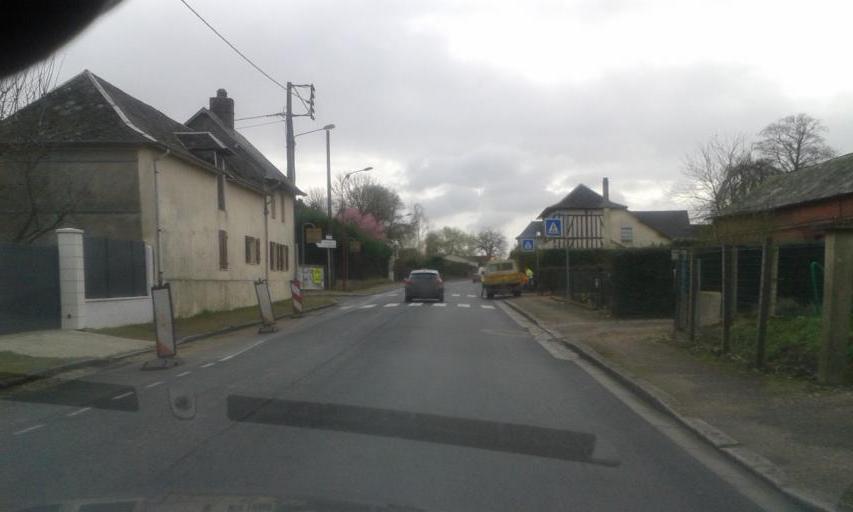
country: FR
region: Haute-Normandie
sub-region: Departement de l'Eure
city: Fleury-sur-Andelle
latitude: 49.3856
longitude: 1.3105
